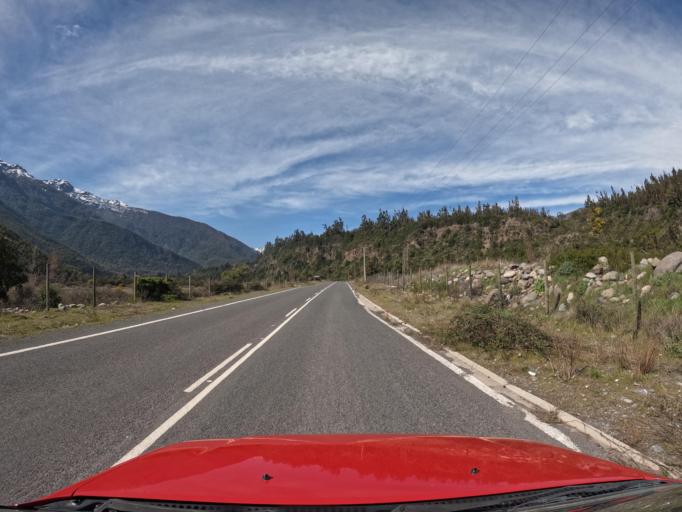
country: CL
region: Maule
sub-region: Provincia de Curico
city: Teno
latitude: -35.0040
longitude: -70.8306
